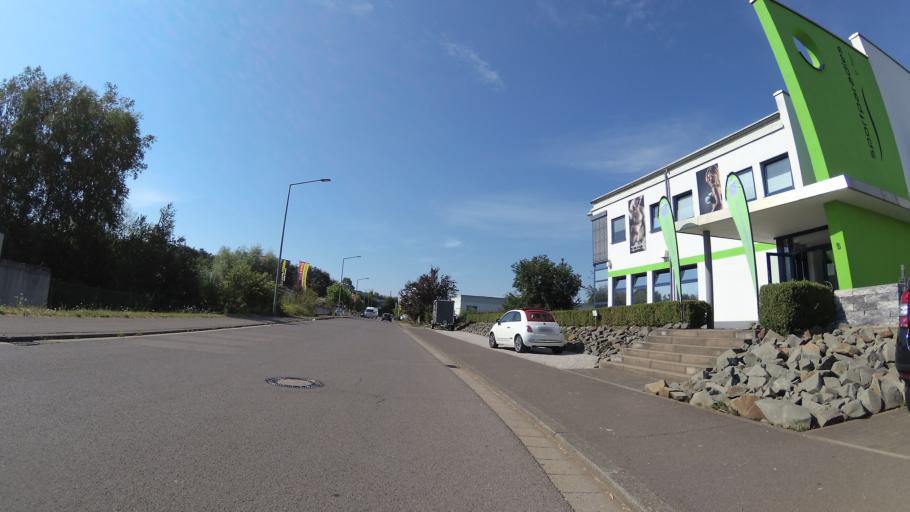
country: DE
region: Saarland
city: Homburg
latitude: 49.3360
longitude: 7.3430
